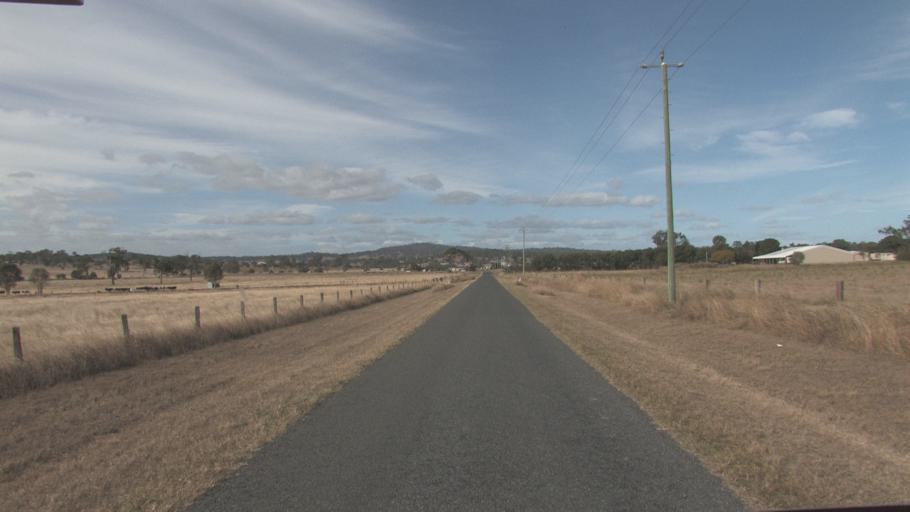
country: AU
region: Queensland
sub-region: Logan
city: Cedar Vale
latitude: -27.9233
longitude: 152.9769
